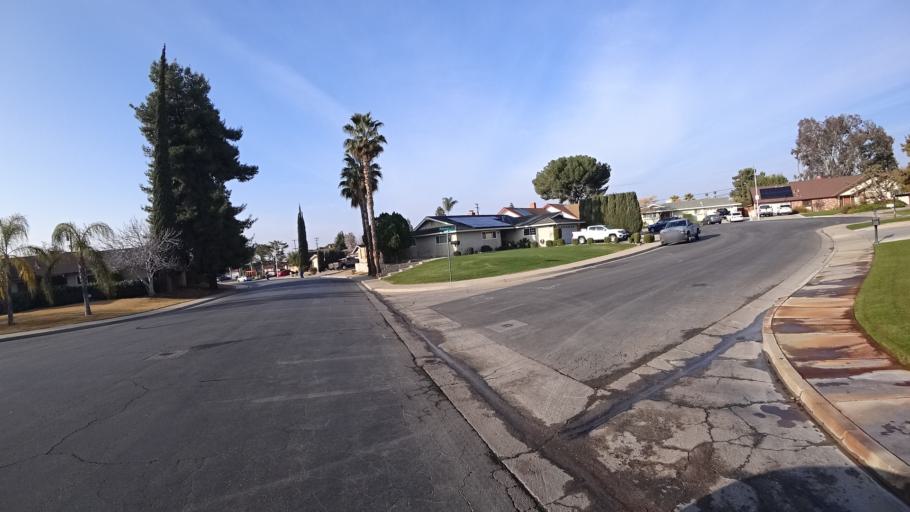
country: US
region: California
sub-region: Kern County
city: Oildale
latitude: 35.4004
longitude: -118.9480
